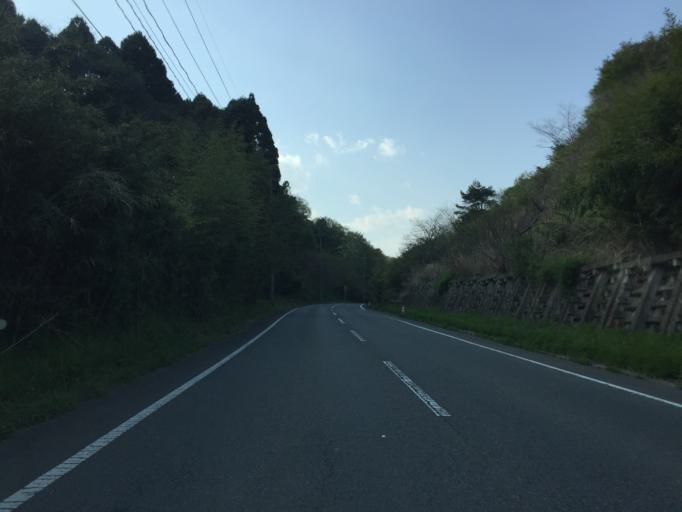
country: JP
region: Fukushima
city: Iwaki
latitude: 36.9693
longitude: 140.8390
